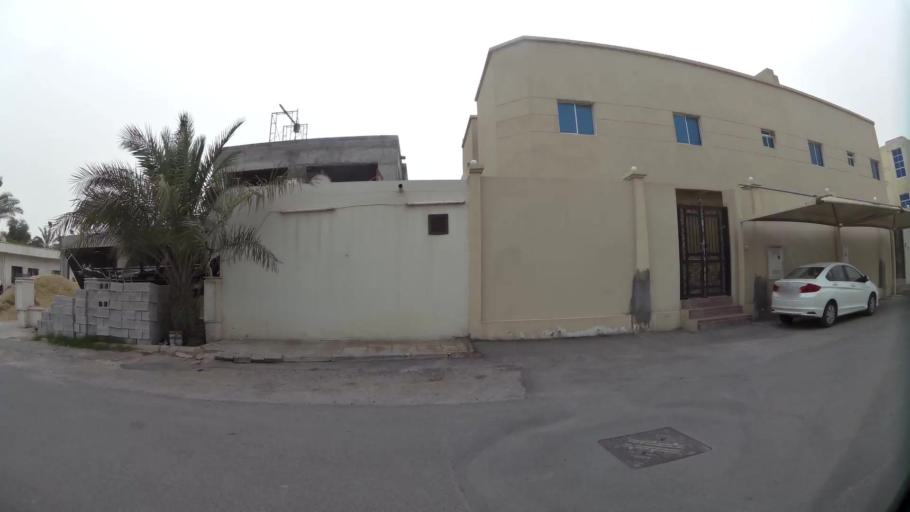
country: QA
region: Baladiyat ad Dawhah
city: Doha
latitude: 25.2597
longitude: 51.4921
